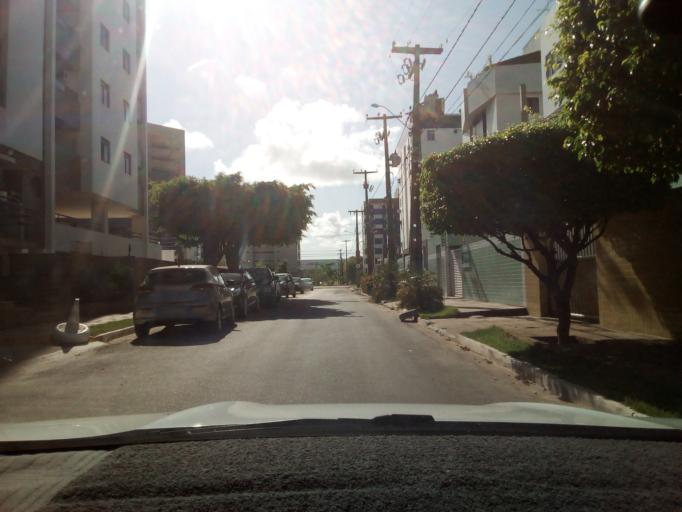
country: BR
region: Paraiba
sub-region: Cabedelo
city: Cabedelo
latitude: -7.0418
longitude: -34.8427
